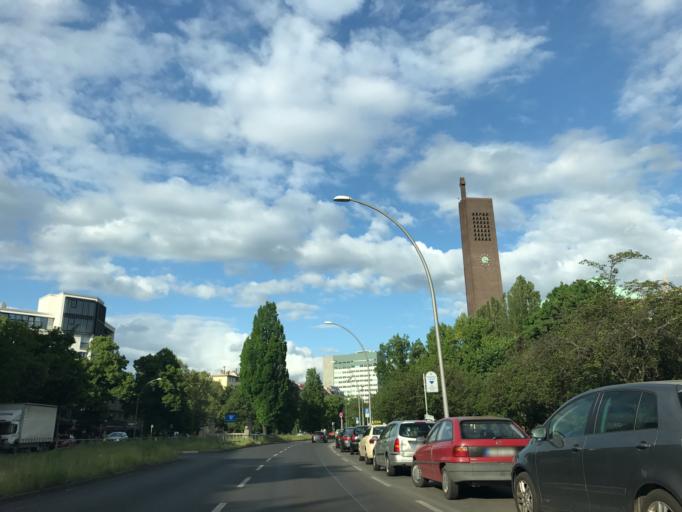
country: DE
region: Berlin
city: Wilmersdorf Bezirk
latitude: 52.4941
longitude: 13.3250
